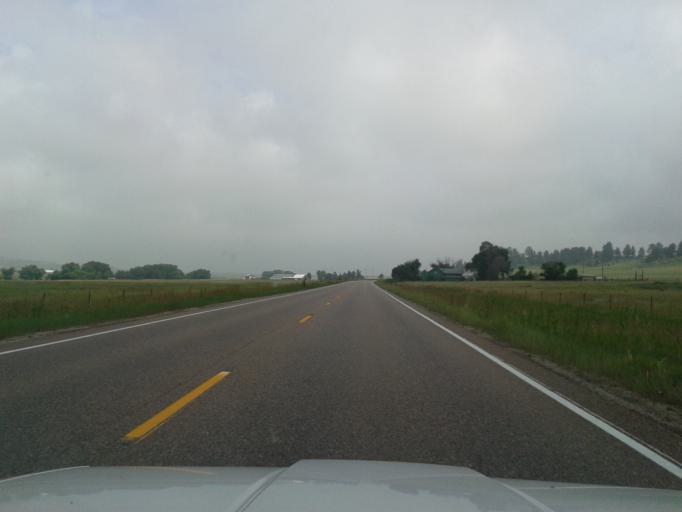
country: US
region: Colorado
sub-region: Elbert County
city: Elizabeth
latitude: 39.2510
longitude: -104.7001
